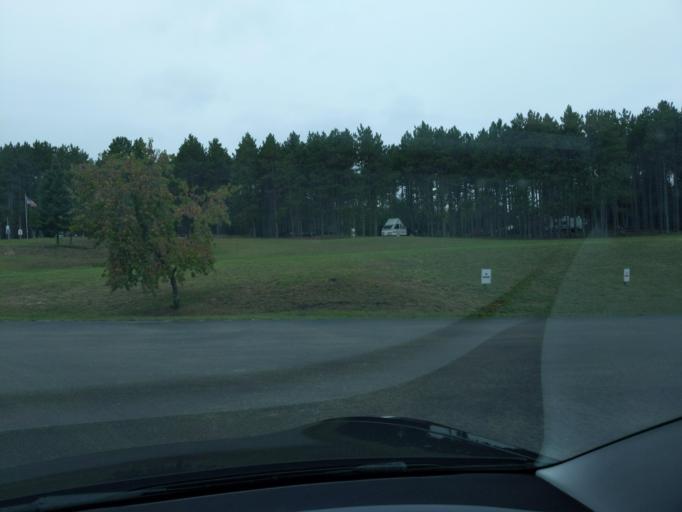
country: US
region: Michigan
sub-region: Antrim County
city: Elk Rapids
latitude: 44.8154
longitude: -85.3870
